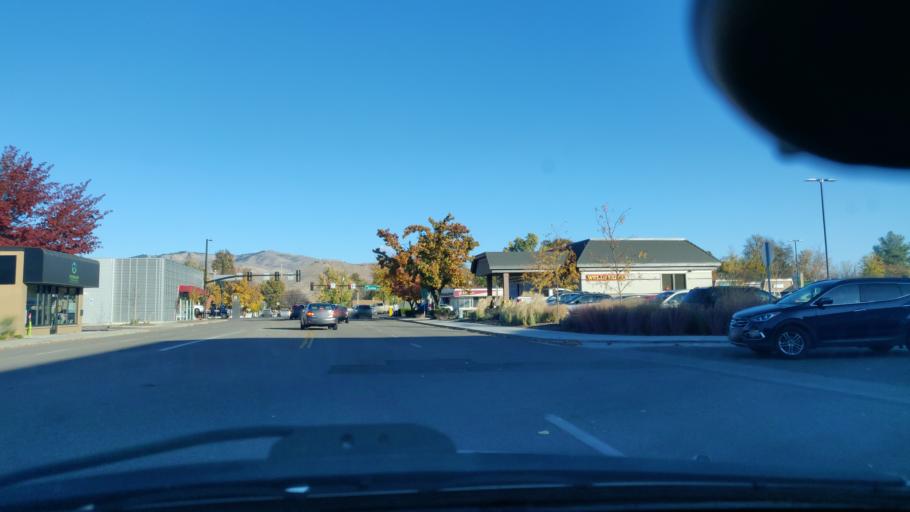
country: US
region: Idaho
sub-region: Ada County
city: Boise
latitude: 43.5984
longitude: -116.1950
